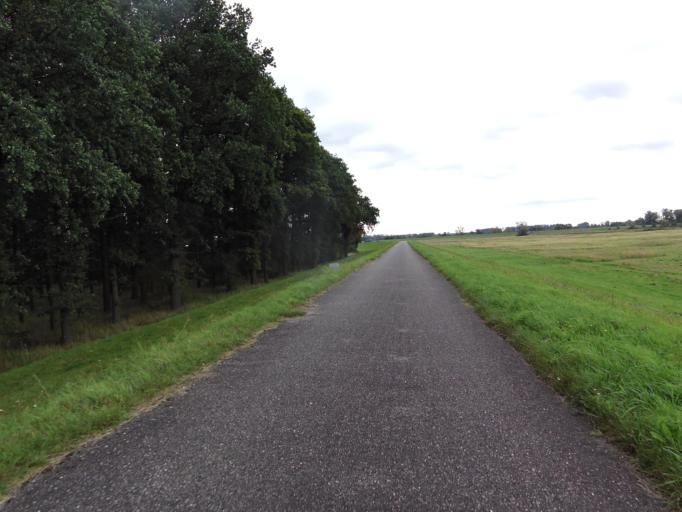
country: DE
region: Brandenburg
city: Bad Wilsnack
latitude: 52.8822
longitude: 11.9735
